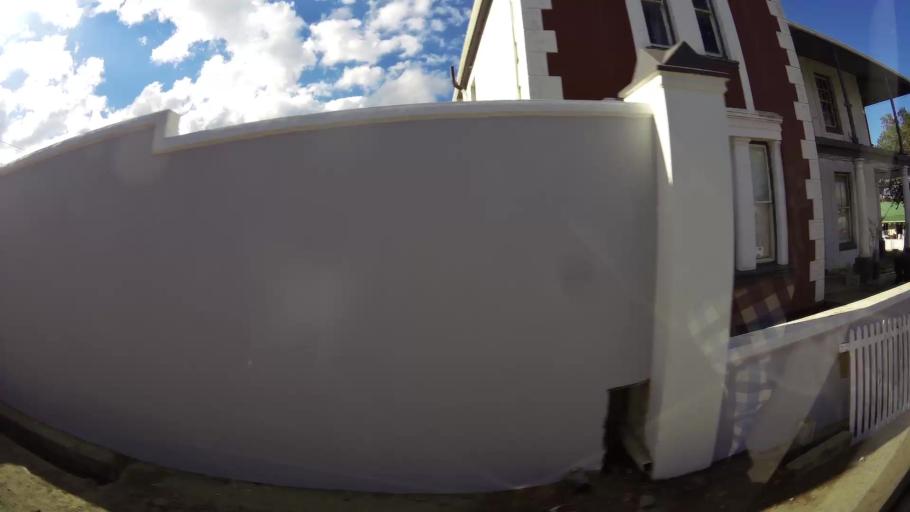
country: ZA
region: Western Cape
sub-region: Overberg District Municipality
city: Swellendam
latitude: -34.0218
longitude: 20.4411
